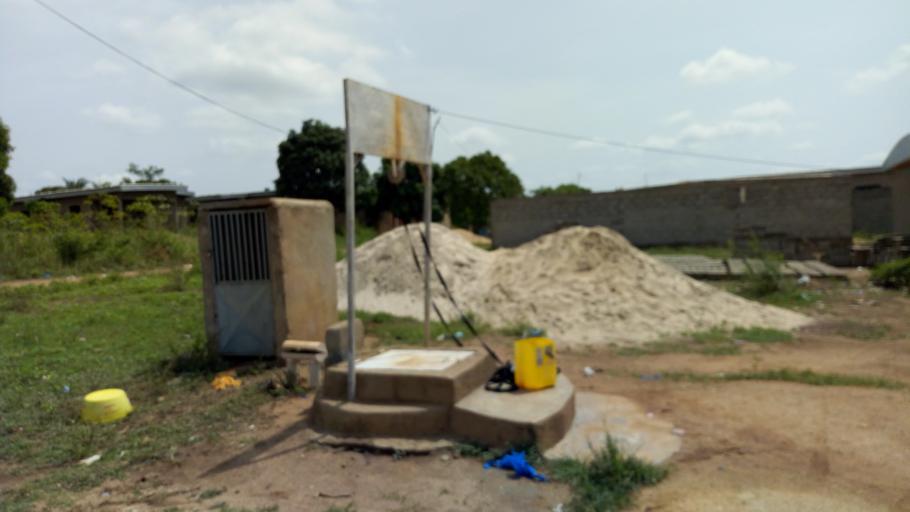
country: CI
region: Vallee du Bandama
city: Bouake
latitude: 7.7270
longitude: -4.9909
